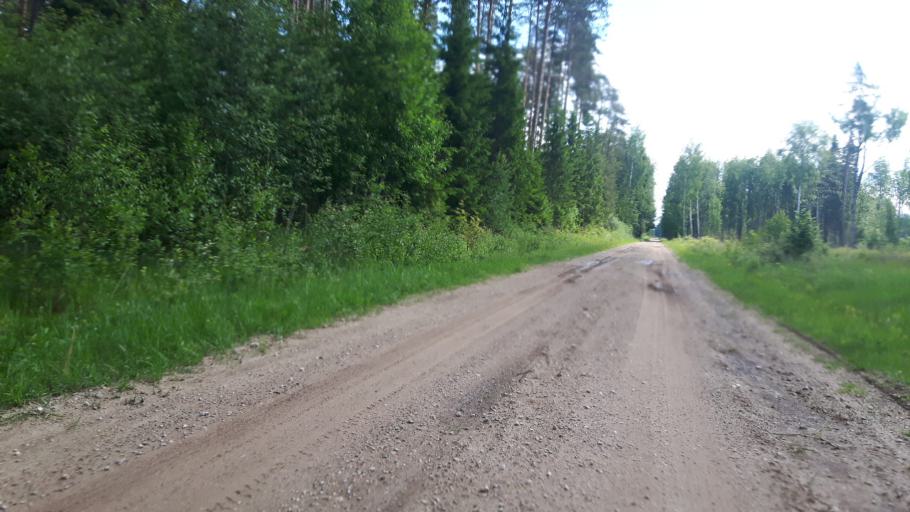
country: EE
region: Paernumaa
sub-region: Vaendra vald (alev)
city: Vandra
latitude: 58.7297
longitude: 25.0209
